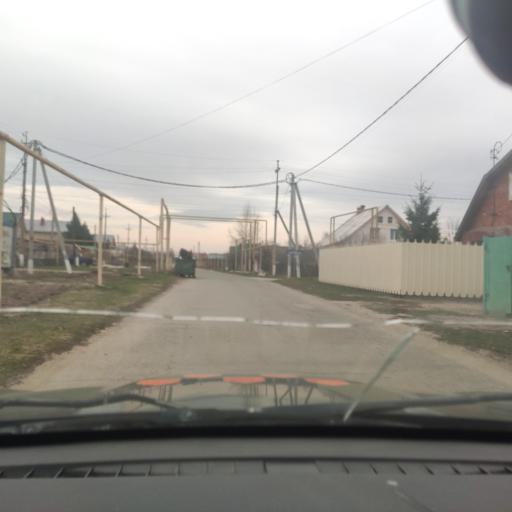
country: RU
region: Samara
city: Podstepki
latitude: 53.5135
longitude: 49.1369
